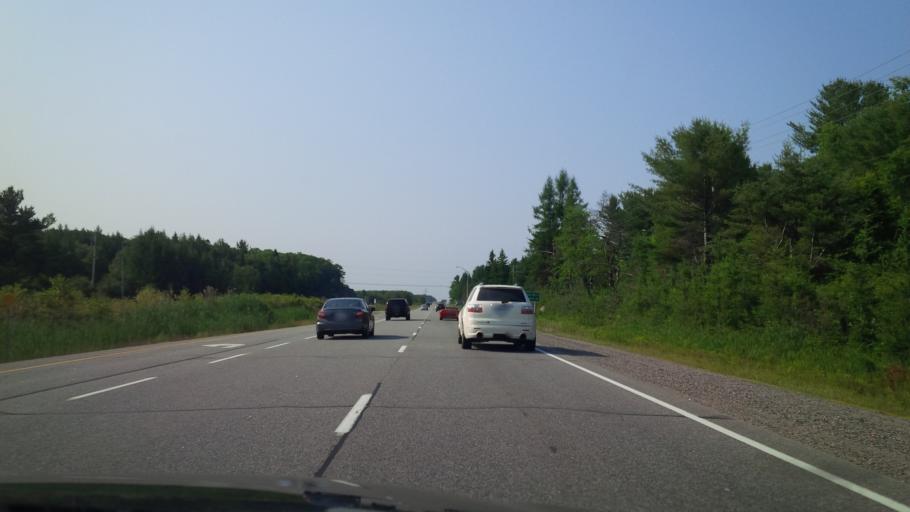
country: CA
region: Ontario
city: Bracebridge
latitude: 45.1782
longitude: -79.3124
